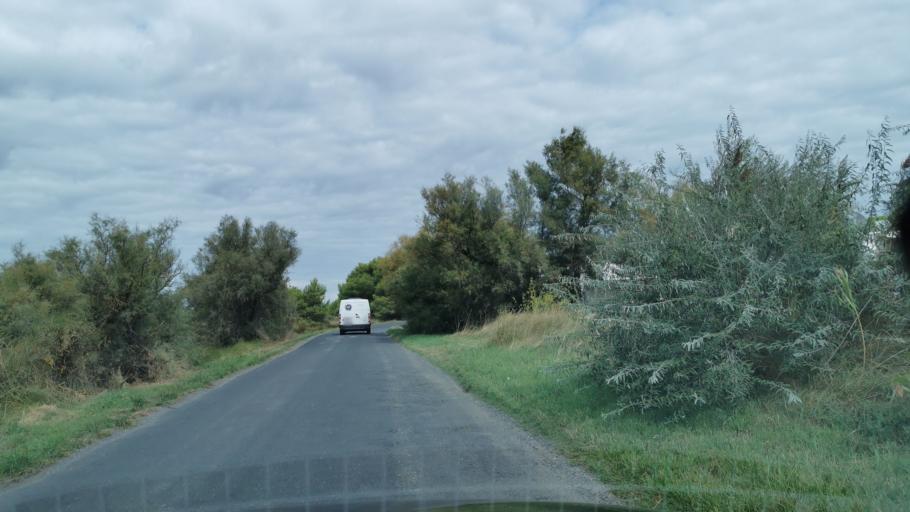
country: FR
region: Languedoc-Roussillon
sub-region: Departement de l'Aude
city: Fleury
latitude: 43.1903
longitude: 3.1965
